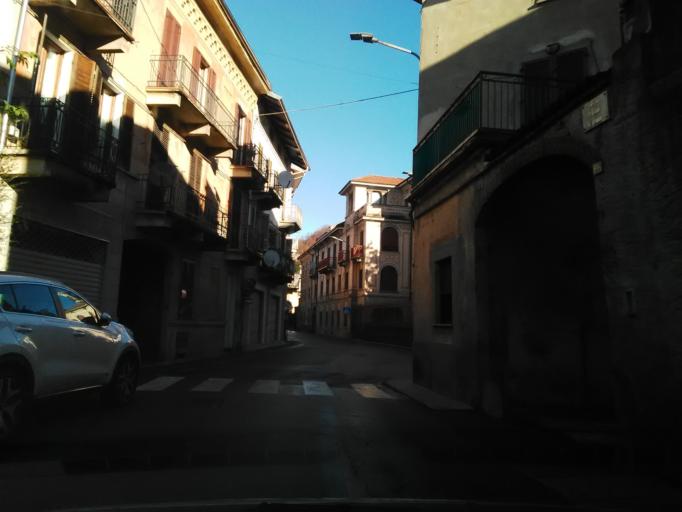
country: IT
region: Piedmont
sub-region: Provincia di Vercelli
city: Quarona
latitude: 45.7639
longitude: 8.2688
